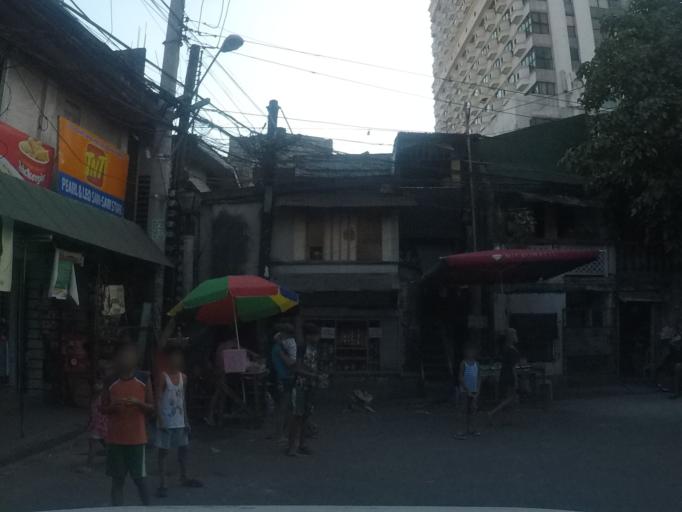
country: PH
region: Metro Manila
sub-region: San Juan
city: San Juan
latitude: 14.6073
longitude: 121.0492
